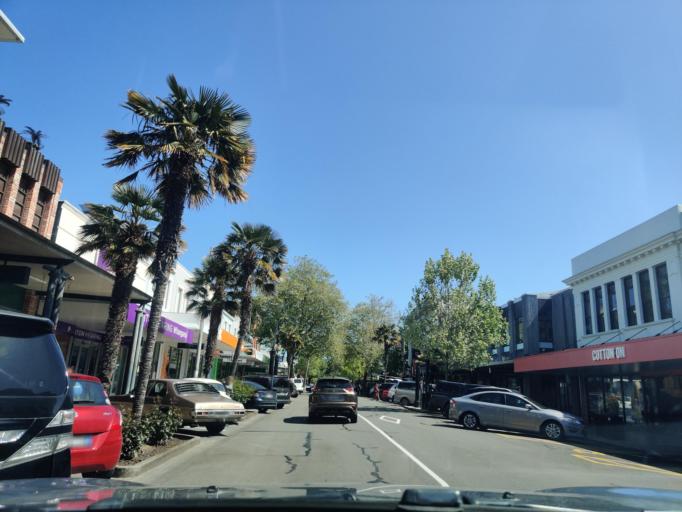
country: NZ
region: Manawatu-Wanganui
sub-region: Wanganui District
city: Wanganui
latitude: -39.9333
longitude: 175.0528
